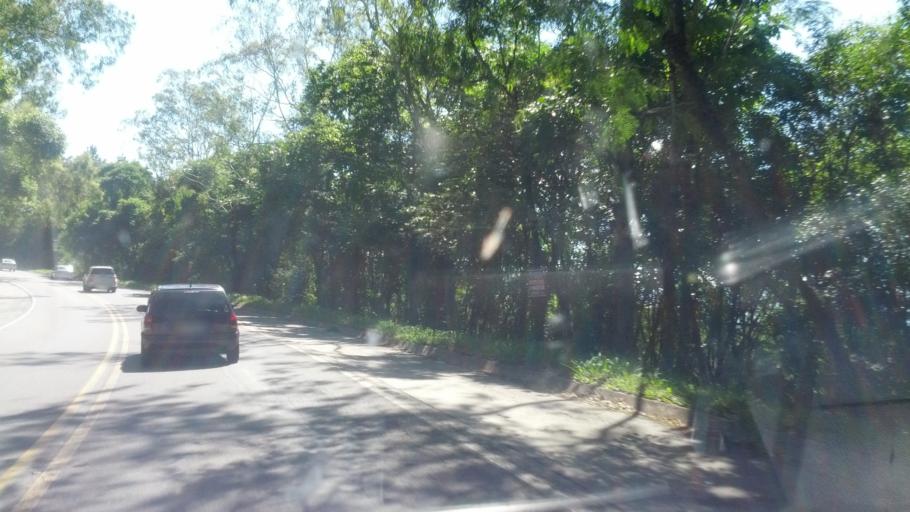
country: BR
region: Santa Catarina
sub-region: Rio Do Sul
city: Rio do Sul
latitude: -27.1692
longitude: -49.5625
